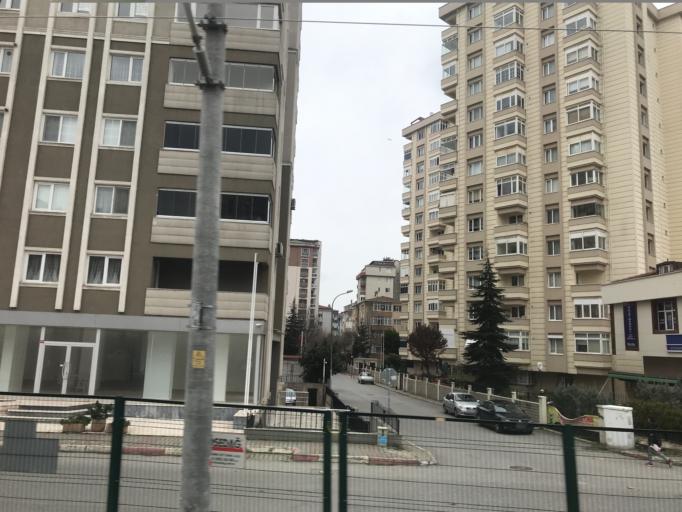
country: TR
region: Istanbul
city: Maltepe
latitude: 40.9005
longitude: 29.1670
